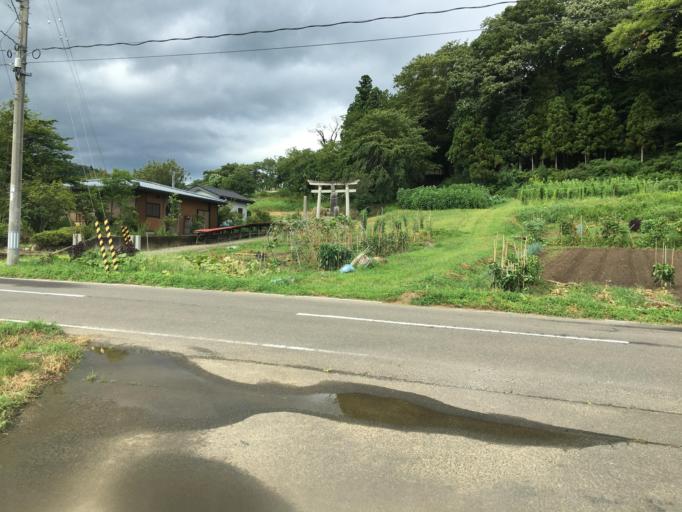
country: JP
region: Fukushima
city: Nihommatsu
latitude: 37.5661
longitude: 140.4168
